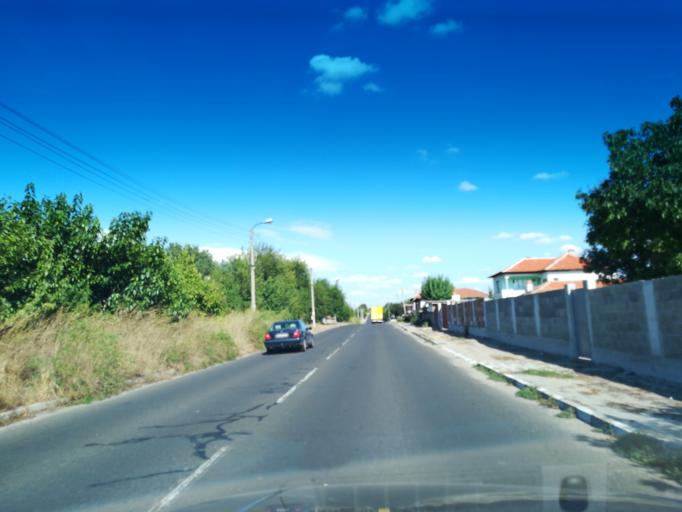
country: BG
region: Stara Zagora
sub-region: Obshtina Chirpan
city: Chirpan
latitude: 42.0588
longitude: 25.2690
